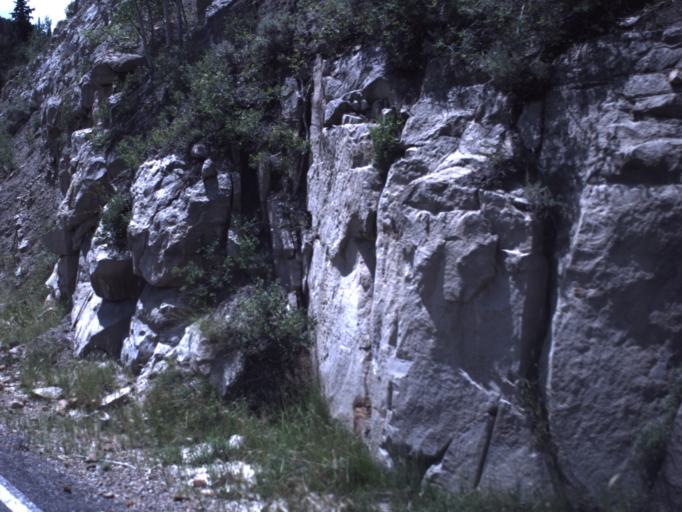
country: US
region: Utah
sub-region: Sanpete County
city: Fairview
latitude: 39.6678
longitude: -111.1535
